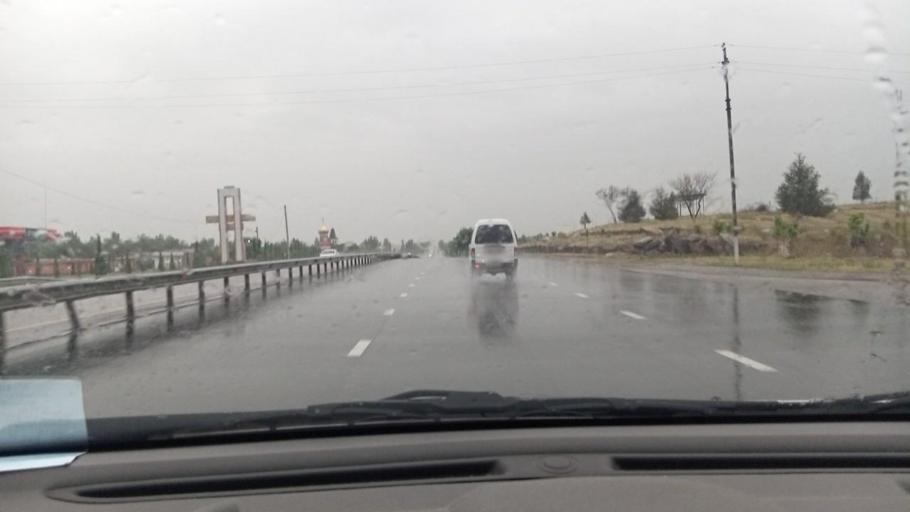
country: UZ
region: Toshkent
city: Tuytepa
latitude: 41.1234
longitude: 69.4397
